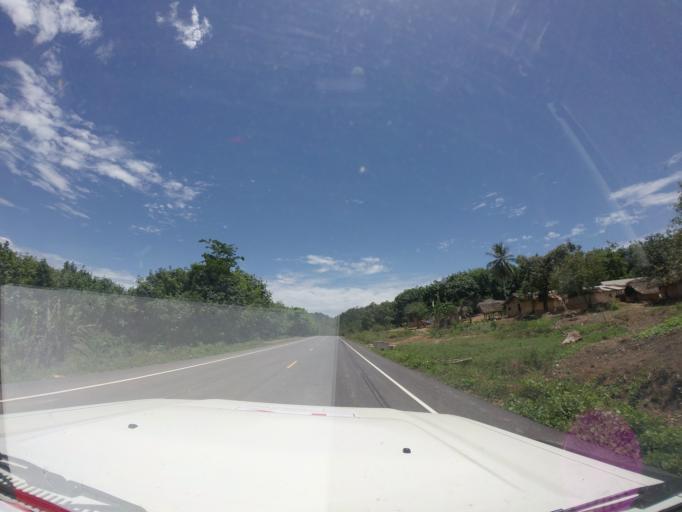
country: LR
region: Margibi
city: Kakata
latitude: 6.7669
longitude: -10.0162
